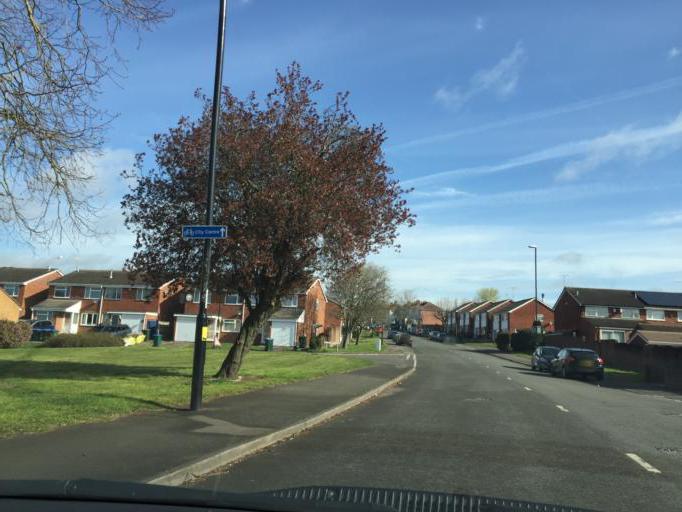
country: GB
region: England
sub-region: Coventry
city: Coventry
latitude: 52.3887
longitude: -1.4980
